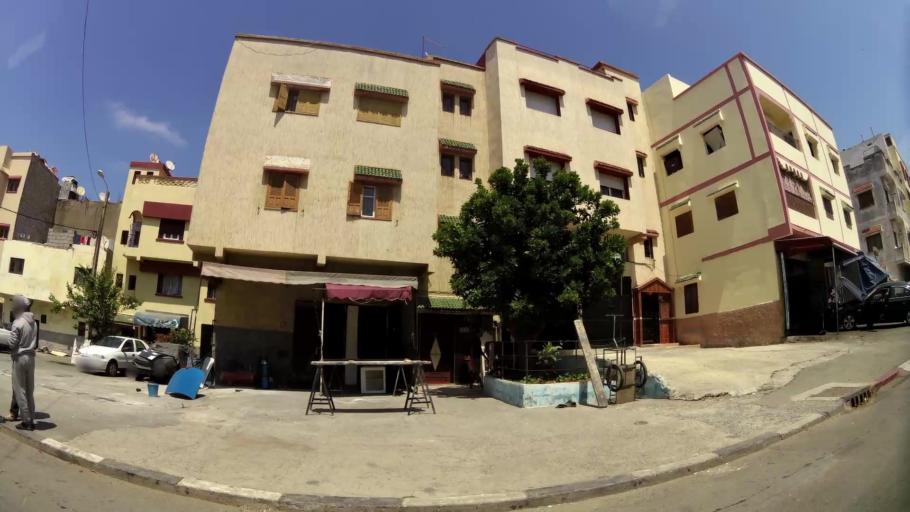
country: MA
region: Rabat-Sale-Zemmour-Zaer
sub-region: Skhirate-Temara
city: Temara
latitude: 33.9696
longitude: -6.8936
